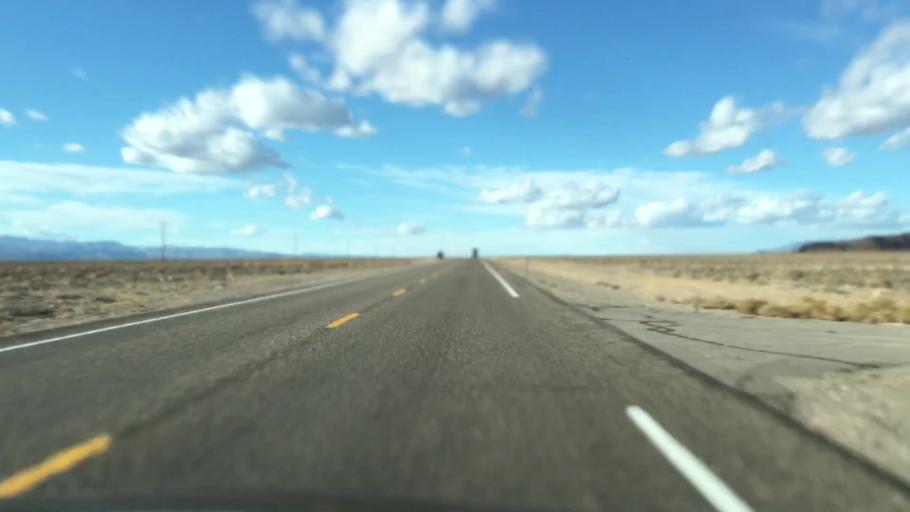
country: US
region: Nevada
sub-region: Nye County
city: Beatty
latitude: 37.1933
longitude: -116.9464
